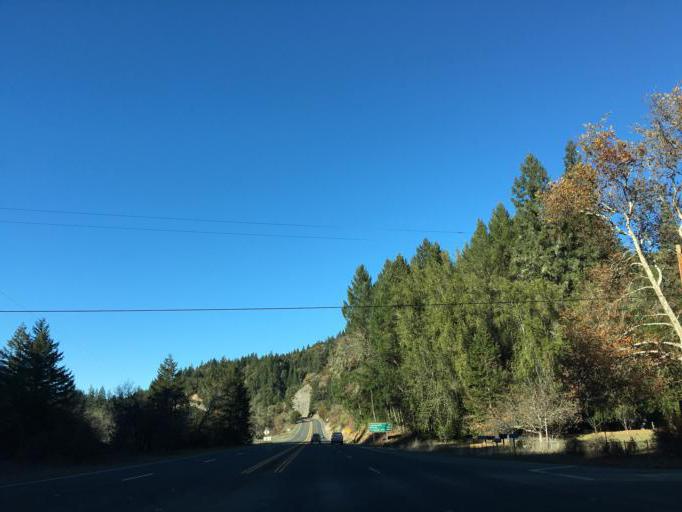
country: US
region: California
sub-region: Mendocino County
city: Brooktrails
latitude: 39.5170
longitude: -123.3909
